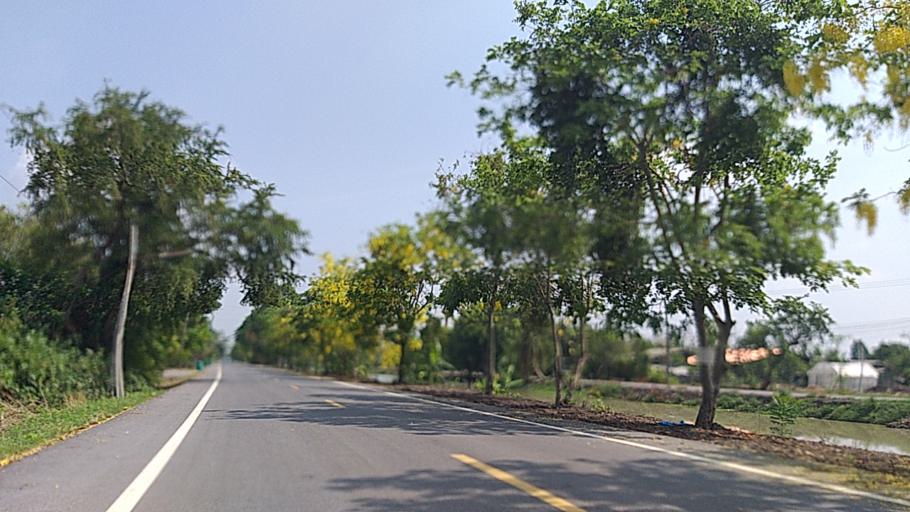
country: TH
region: Pathum Thani
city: Nong Suea
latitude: 14.2182
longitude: 100.8457
